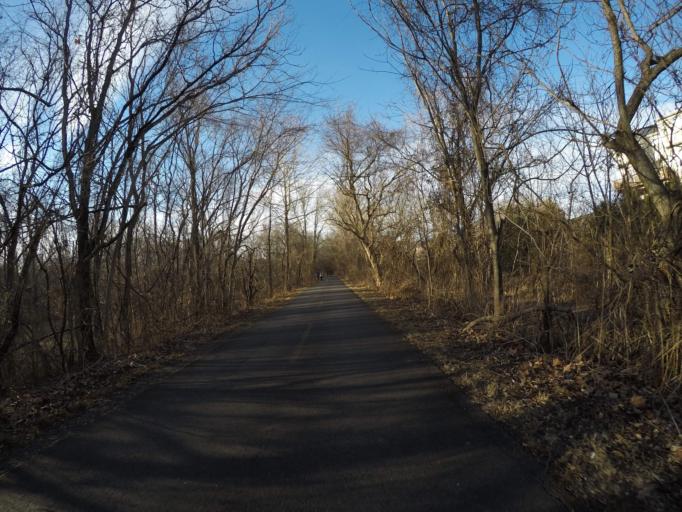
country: US
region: Virginia
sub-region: Loudoun County
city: Leesburg
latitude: 39.1023
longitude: -77.5492
